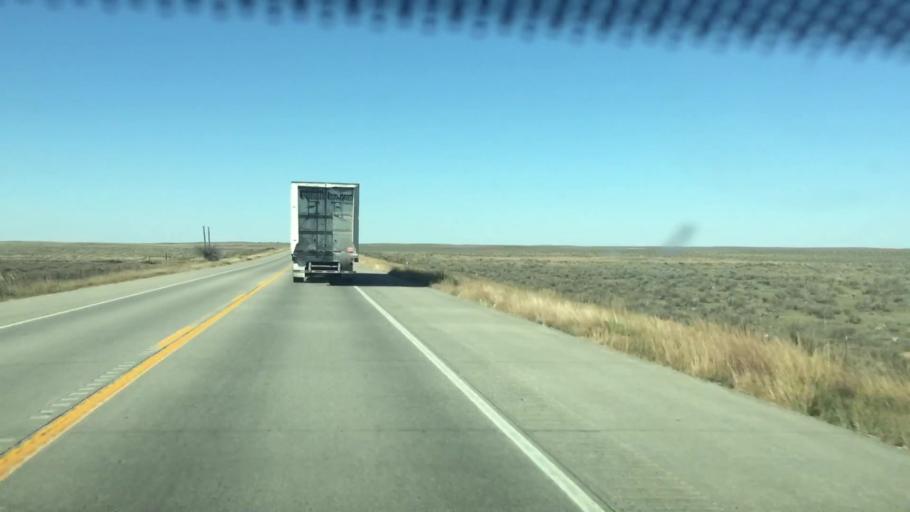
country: US
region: Colorado
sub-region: Kiowa County
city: Eads
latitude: 38.5551
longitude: -102.7860
